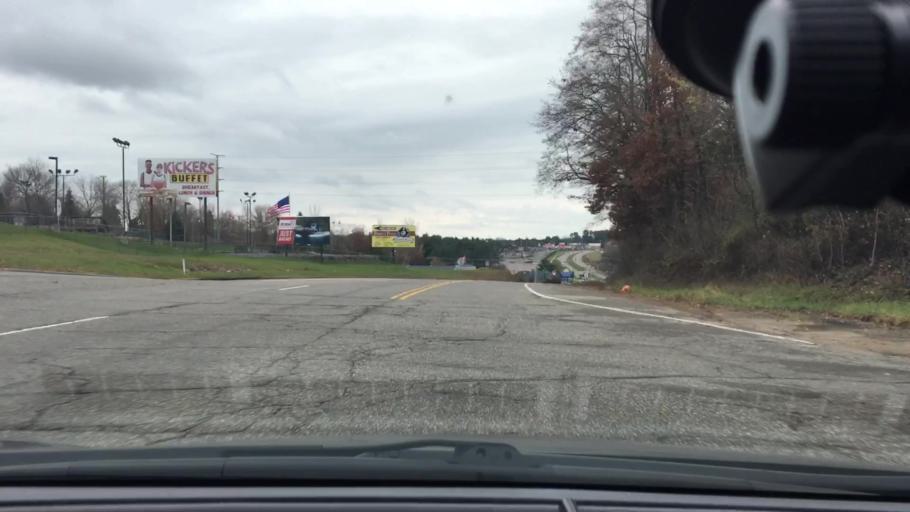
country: US
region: Wisconsin
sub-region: Columbia County
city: Wisconsin Dells
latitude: 43.6301
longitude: -89.7877
